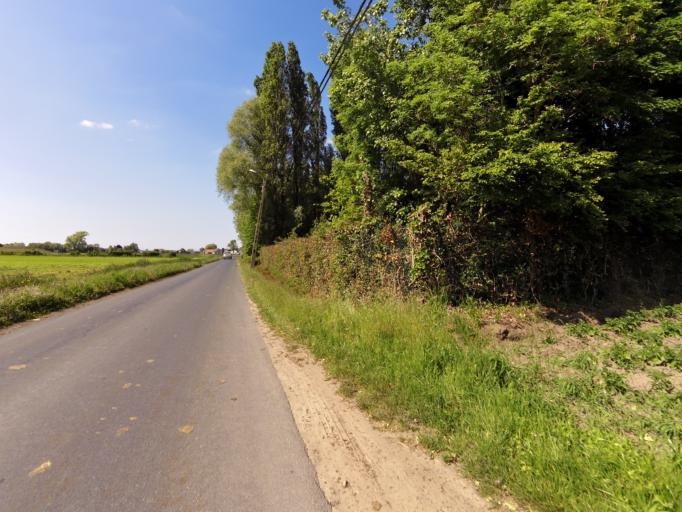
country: BE
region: Flanders
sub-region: Provincie West-Vlaanderen
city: Koekelare
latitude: 51.0766
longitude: 2.9454
